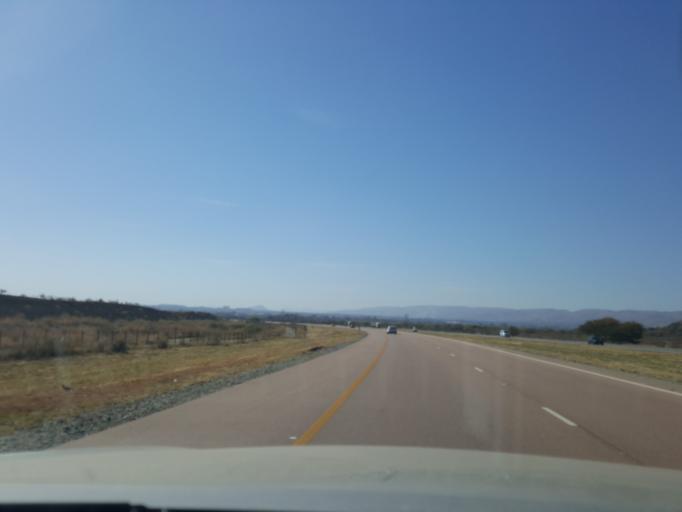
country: ZA
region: North-West
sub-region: Bojanala Platinum District Municipality
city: Brits
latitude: -25.7470
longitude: 27.5195
